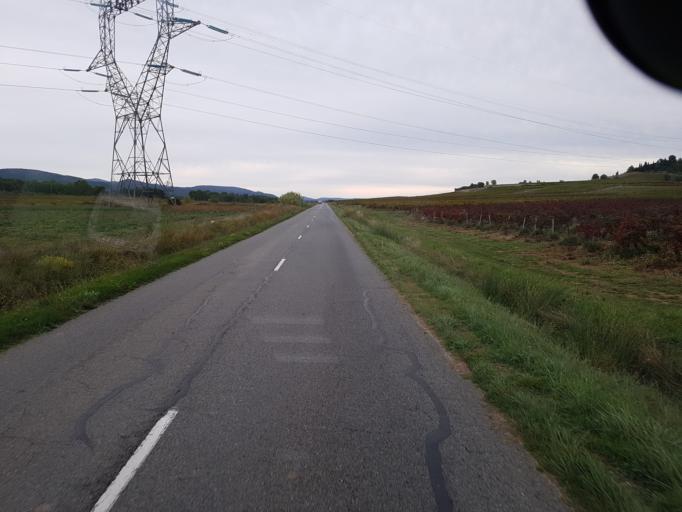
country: FR
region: Languedoc-Roussillon
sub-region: Departement de l'Aude
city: Laure-Minervois
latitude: 43.3029
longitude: 2.4720
